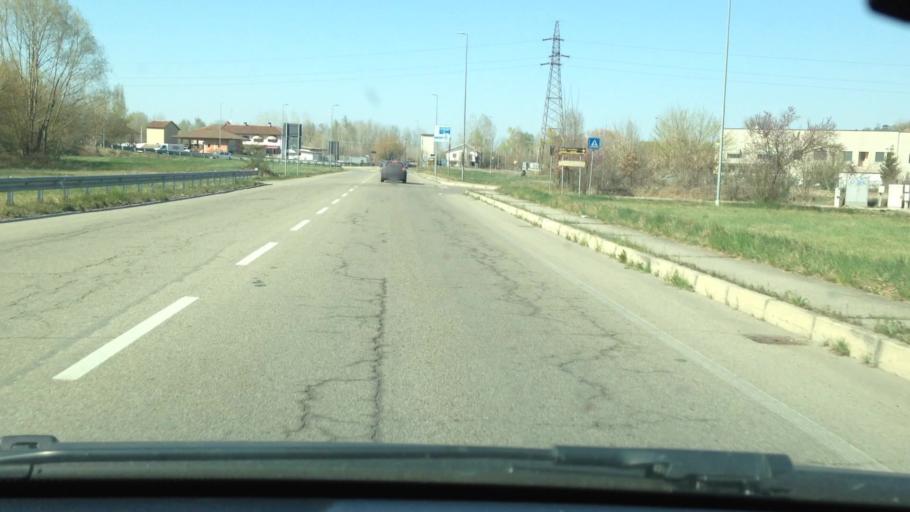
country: IT
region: Piedmont
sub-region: Provincia di Asti
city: Asti
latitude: 44.9189
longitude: 8.2285
